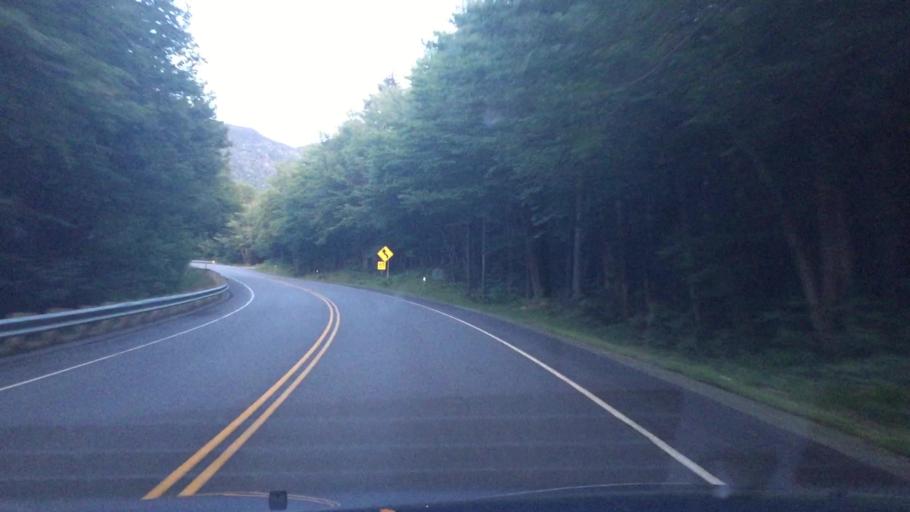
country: US
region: New Hampshire
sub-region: Grafton County
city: Woodstock
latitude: 44.0305
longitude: -71.5230
